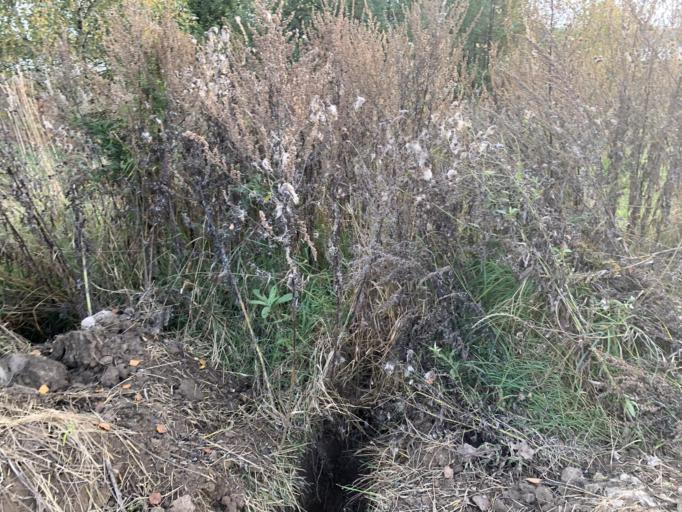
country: RU
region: Jaroslavl
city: Petrovsk
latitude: 56.9793
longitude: 39.3788
